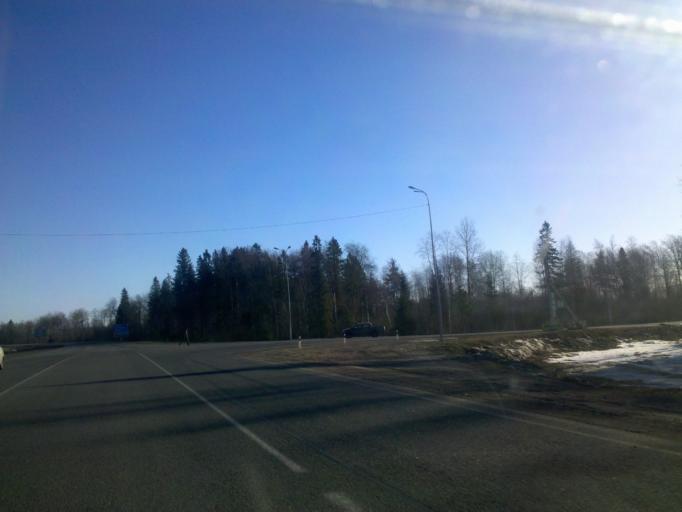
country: RU
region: Republic of Karelia
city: Shuya
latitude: 61.8704
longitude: 34.2283
